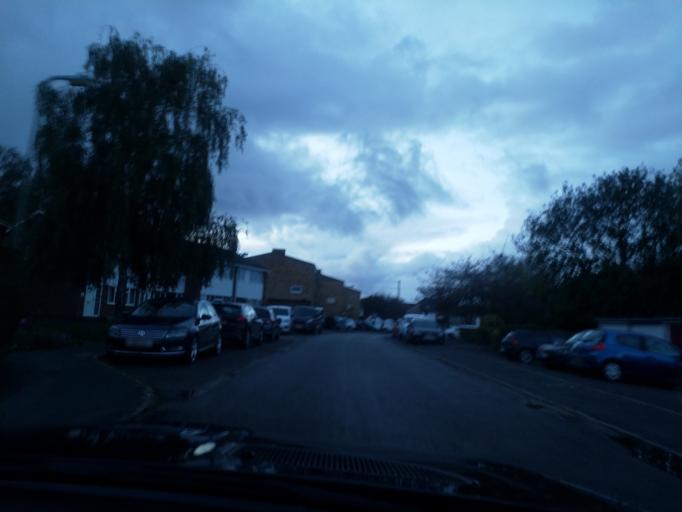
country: GB
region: England
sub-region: Oxfordshire
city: Wheatley
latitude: 51.7452
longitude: -1.1367
